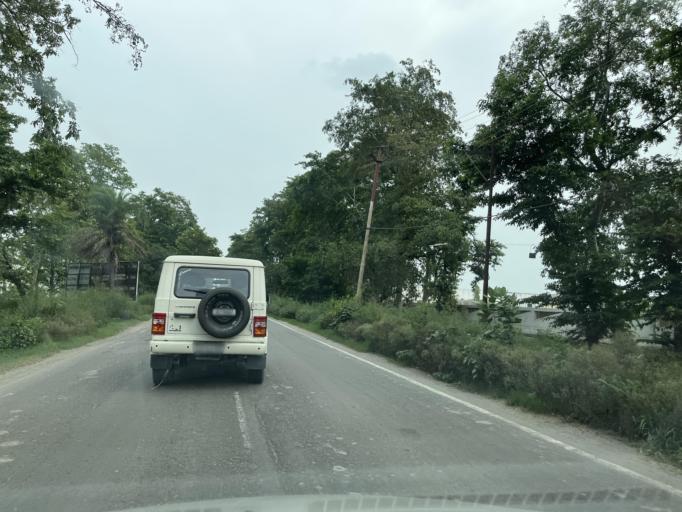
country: IN
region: Uttar Pradesh
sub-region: Rampur
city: Bilaspur
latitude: 29.0281
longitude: 79.2666
